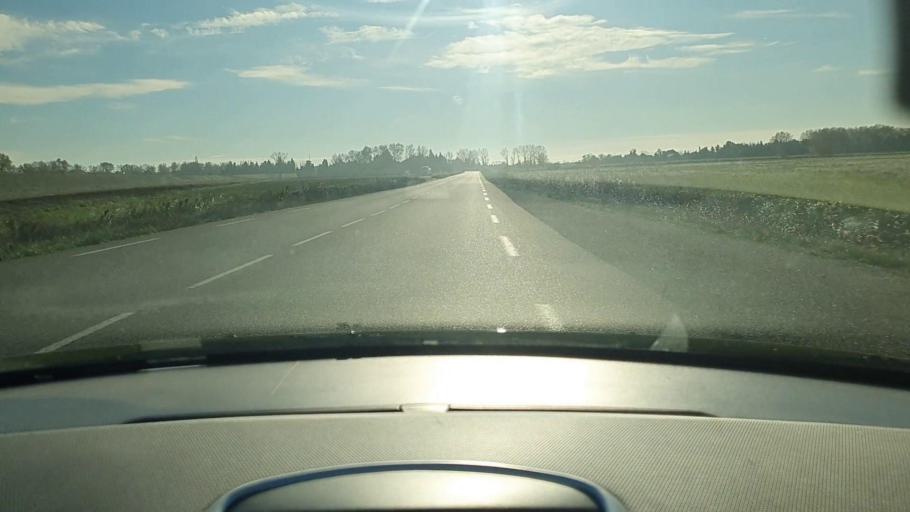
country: FR
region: Languedoc-Roussillon
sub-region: Departement du Gard
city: Fourques
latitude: 43.7446
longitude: 4.6127
